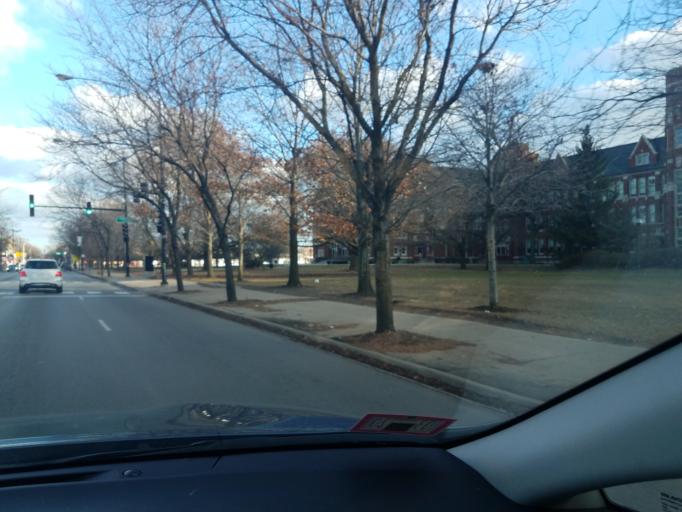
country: US
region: Illinois
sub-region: Cook County
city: Lincolnwood
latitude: 41.9467
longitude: -87.6911
